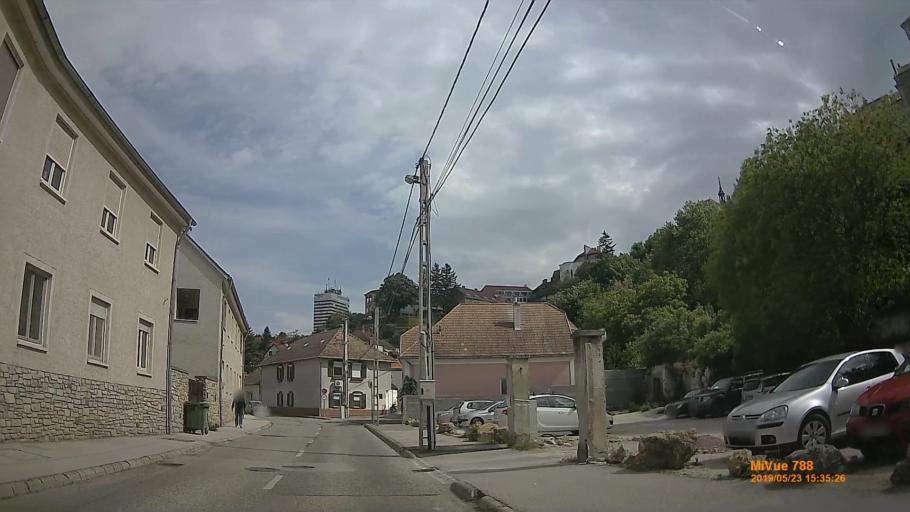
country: HU
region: Veszprem
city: Veszprem
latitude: 47.0967
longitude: 17.9057
